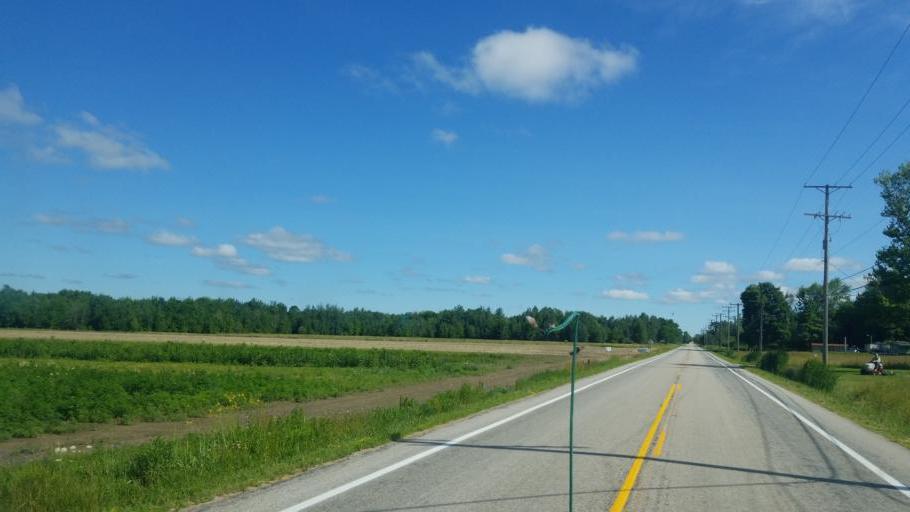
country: US
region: Ohio
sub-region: Ashtabula County
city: Conneaut
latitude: 41.7827
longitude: -80.5721
